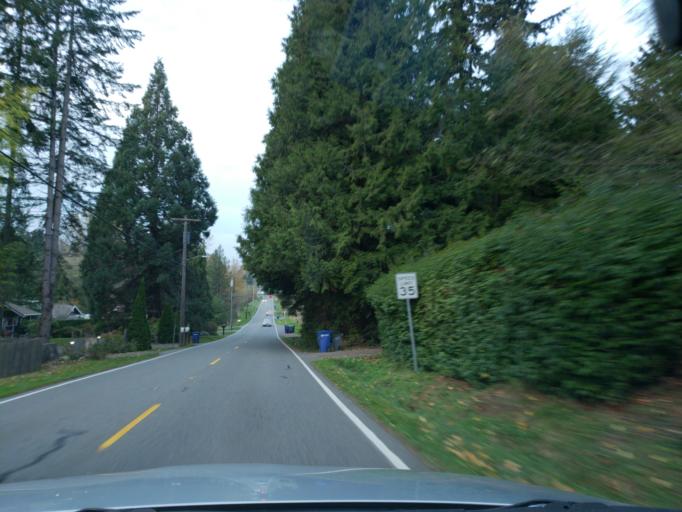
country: US
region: Washington
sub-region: King County
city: Bothell
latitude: 47.7766
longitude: -122.2232
